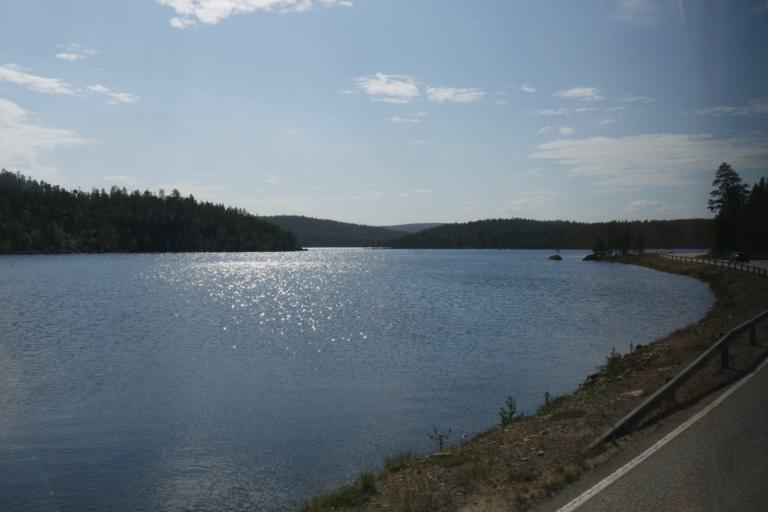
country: FI
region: Lapland
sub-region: Pohjois-Lappi
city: Ivalo
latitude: 68.8164
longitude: 27.3353
